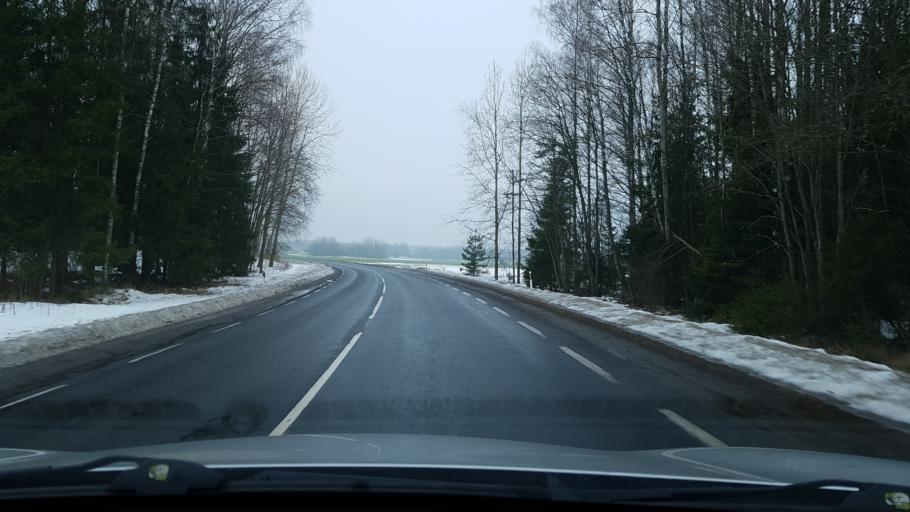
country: EE
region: Valgamaa
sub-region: Torva linn
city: Torva
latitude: 58.2066
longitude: 25.9492
